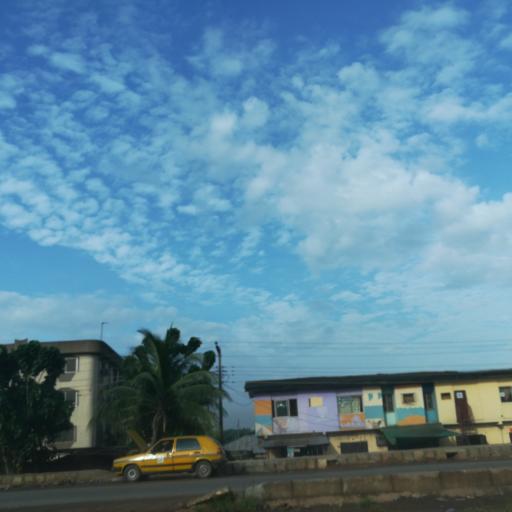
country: NG
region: Lagos
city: Oshodi
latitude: 6.5791
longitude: 3.3423
